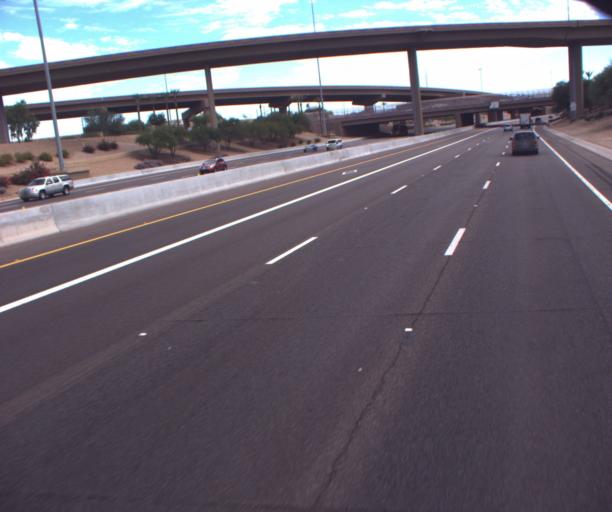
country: US
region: Arizona
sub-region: Maricopa County
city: Chandler
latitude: 33.2919
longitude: -111.8952
